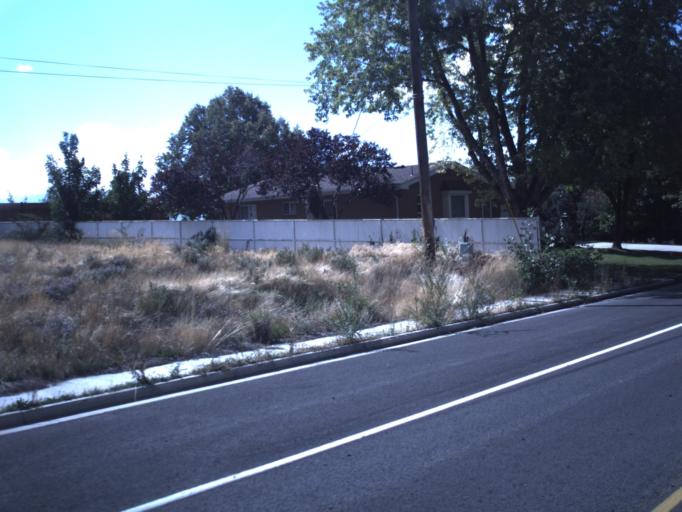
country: US
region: Utah
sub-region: Utah County
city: Mapleton
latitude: 40.1158
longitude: -111.5815
